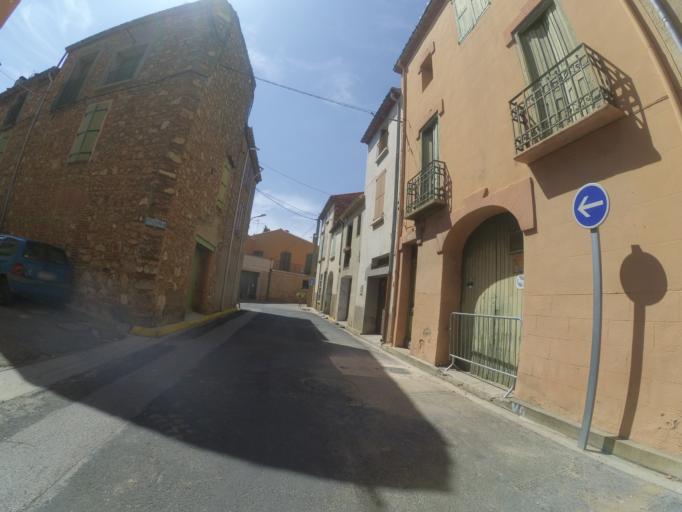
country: FR
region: Languedoc-Roussillon
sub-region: Departement des Pyrenees-Orientales
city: Baixas
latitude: 42.7508
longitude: 2.8079
